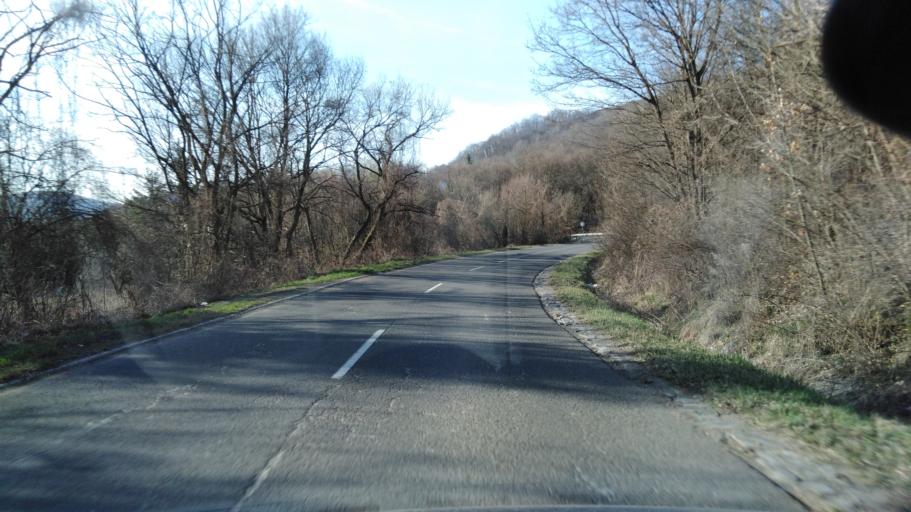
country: HU
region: Nograd
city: Somoskoujfalu
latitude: 48.1601
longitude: 19.8461
